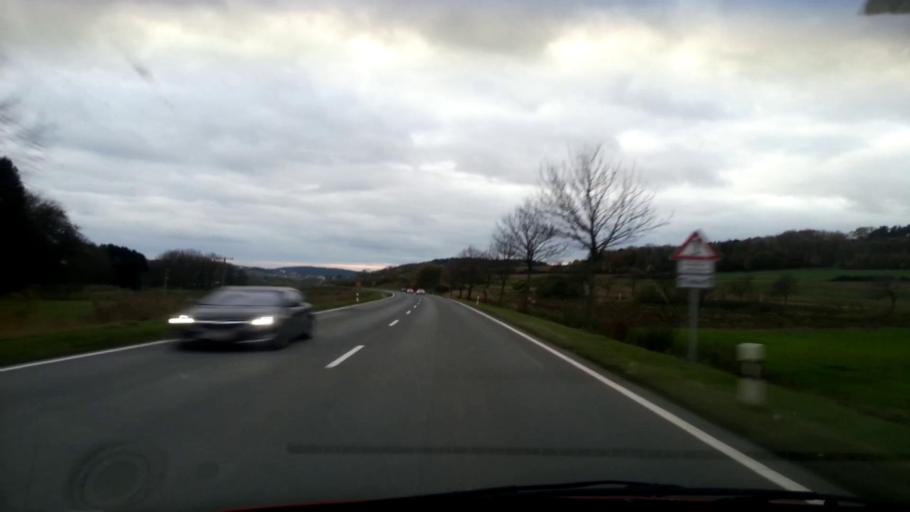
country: DE
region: Bavaria
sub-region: Upper Franconia
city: Kueps Oberfranken
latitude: 50.2130
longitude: 11.2400
